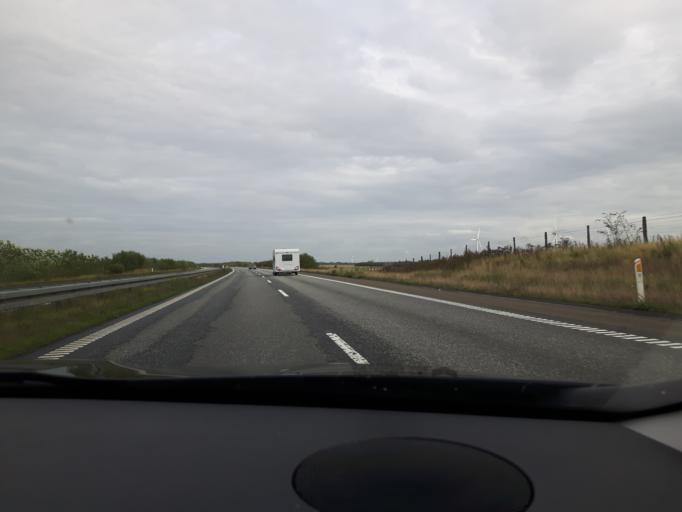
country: DK
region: North Denmark
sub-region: Hjorring Kommune
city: Hjorring
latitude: 57.3992
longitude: 10.0293
